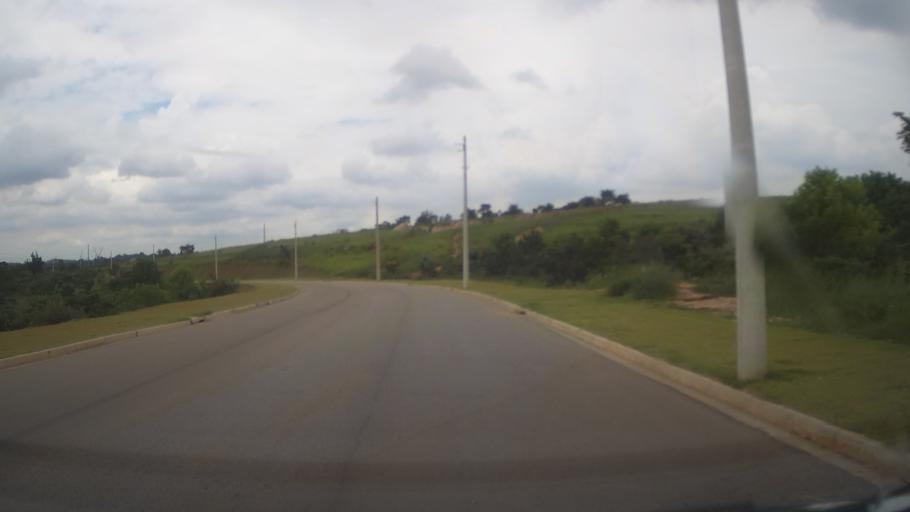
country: BR
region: Sao Paulo
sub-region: Itupeva
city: Itupeva
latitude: -23.1515
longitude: -46.9963
